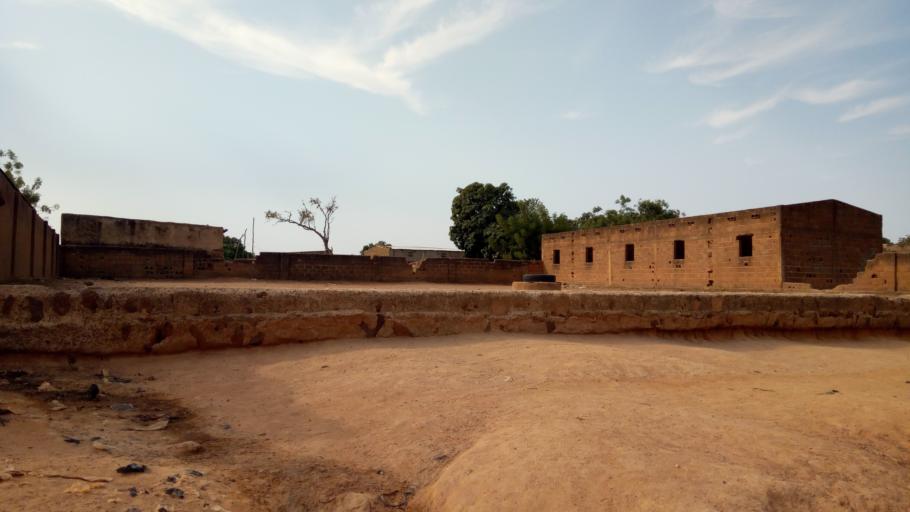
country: ML
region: Sikasso
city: Koutiala
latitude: 12.3840
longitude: -5.4832
